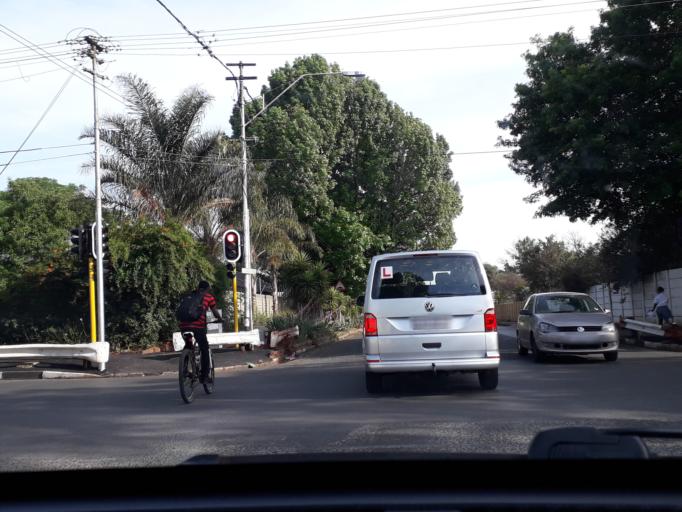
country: ZA
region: Gauteng
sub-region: City of Johannesburg Metropolitan Municipality
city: Johannesburg
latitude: -26.1435
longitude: 28.0895
